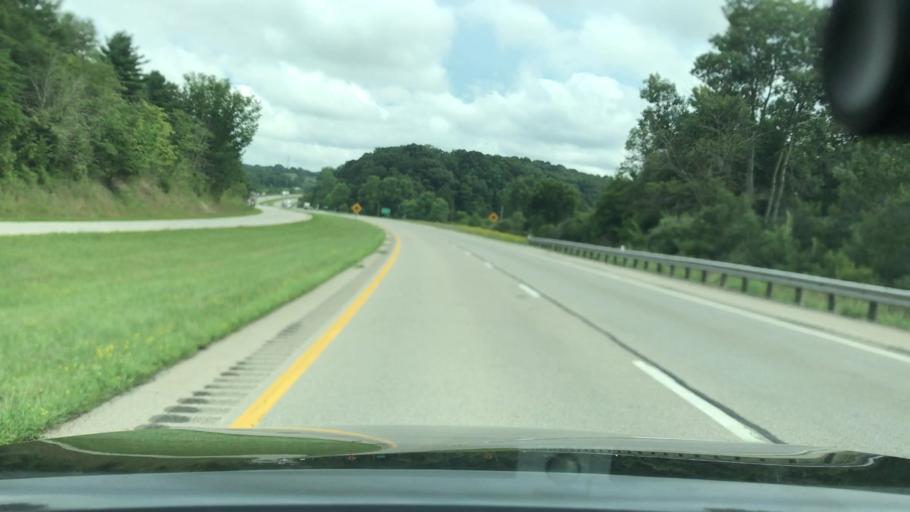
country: US
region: Ohio
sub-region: Jackson County
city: Oak Hill
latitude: 38.9548
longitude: -82.4890
